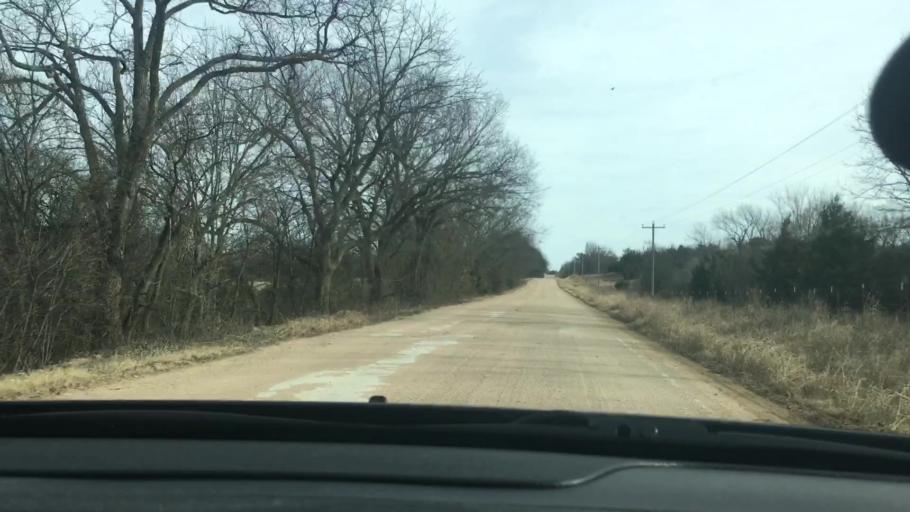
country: US
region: Oklahoma
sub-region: Murray County
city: Sulphur
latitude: 34.4061
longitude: -96.9416
